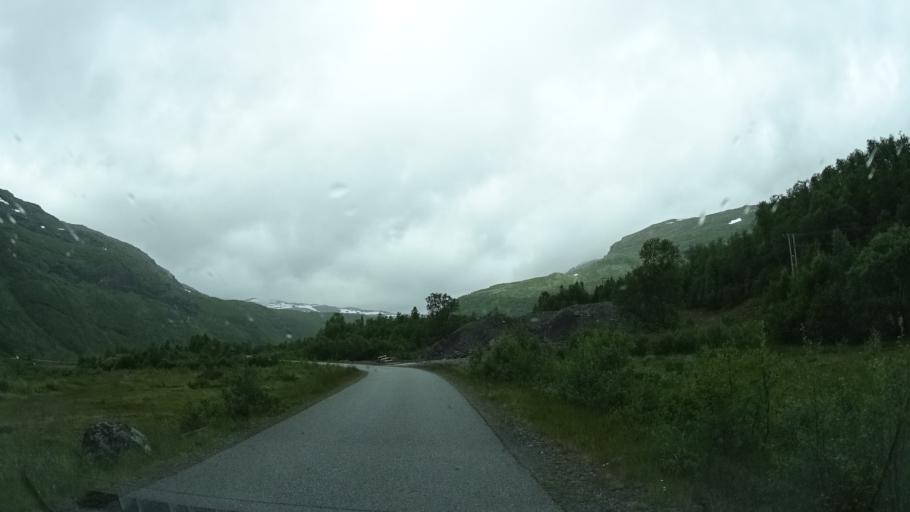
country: NO
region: Sogn og Fjordane
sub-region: Laerdal
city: Laerdalsoyri
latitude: 60.8275
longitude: 7.5136
